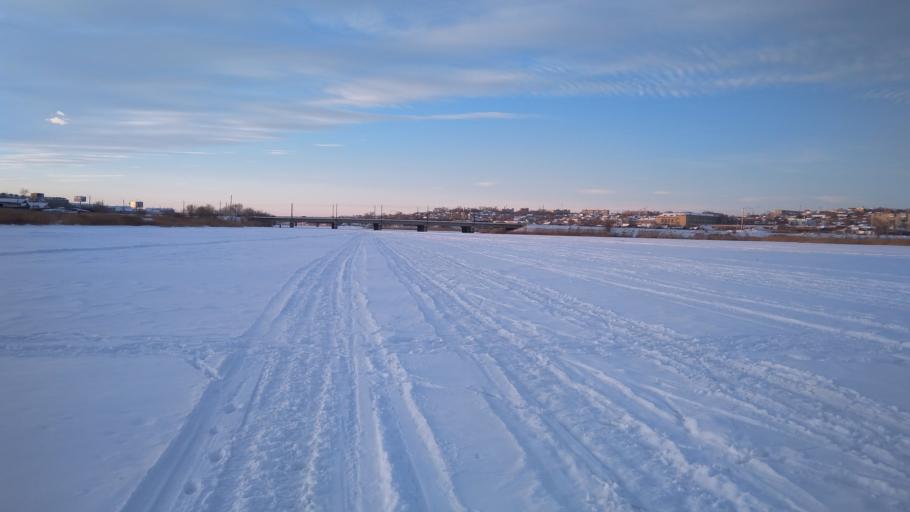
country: RU
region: Chelyabinsk
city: Troitsk
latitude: 54.0894
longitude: 61.5802
